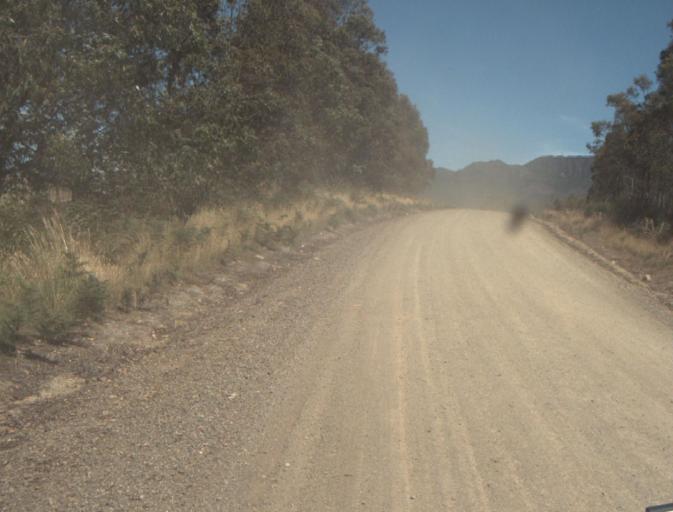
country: AU
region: Tasmania
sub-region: Dorset
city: Scottsdale
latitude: -41.3229
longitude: 147.4458
